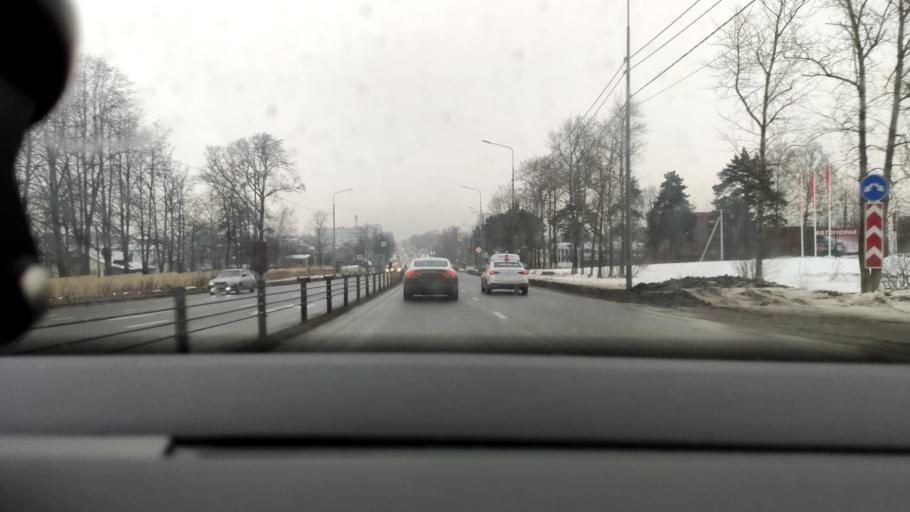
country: RU
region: Moskovskaya
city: Sergiyev Posad
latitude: 56.2775
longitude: 38.1227
